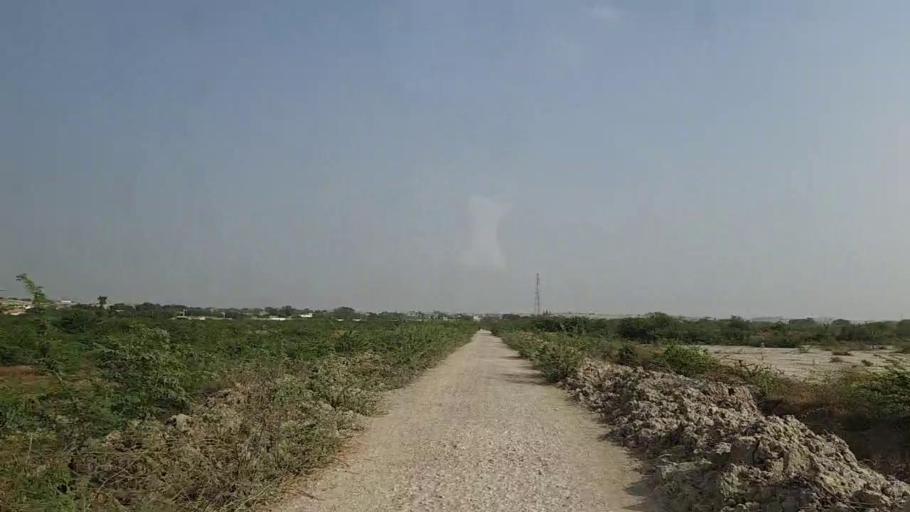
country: PK
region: Sindh
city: Naukot
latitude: 24.6619
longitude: 69.2851
